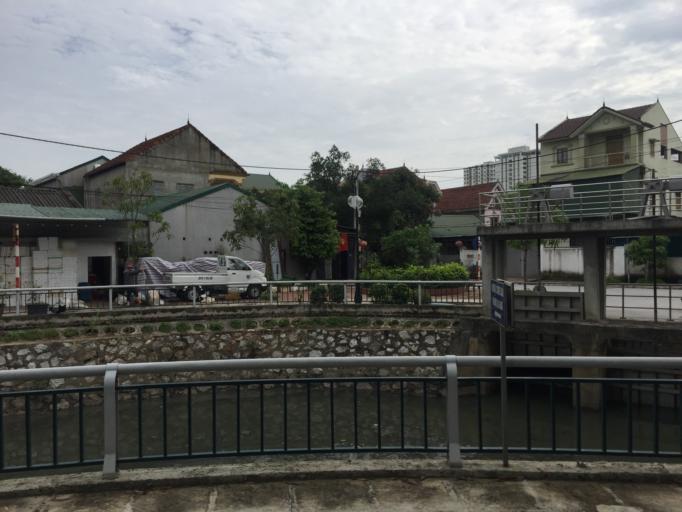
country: VN
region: Nghe An
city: Yen Vinh
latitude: 18.6734
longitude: 105.6712
